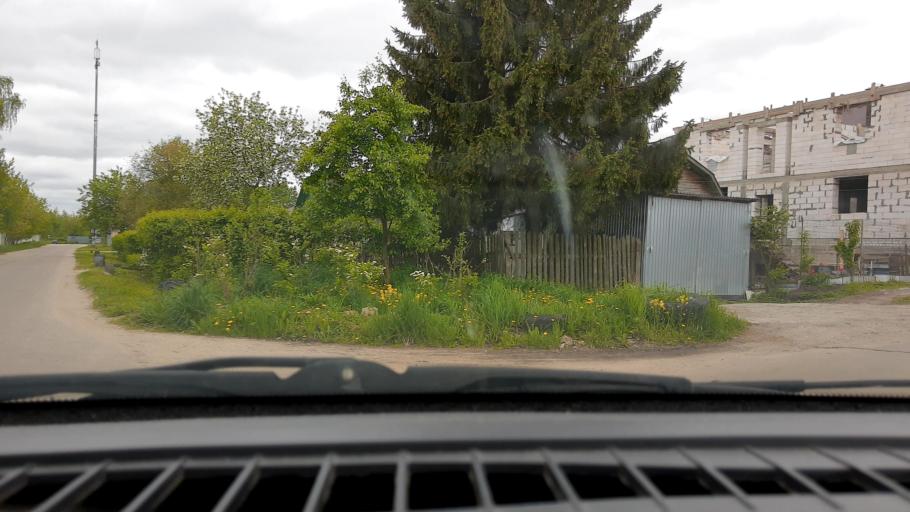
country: RU
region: Nizjnij Novgorod
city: Gorbatovka
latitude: 56.3832
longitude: 43.7792
